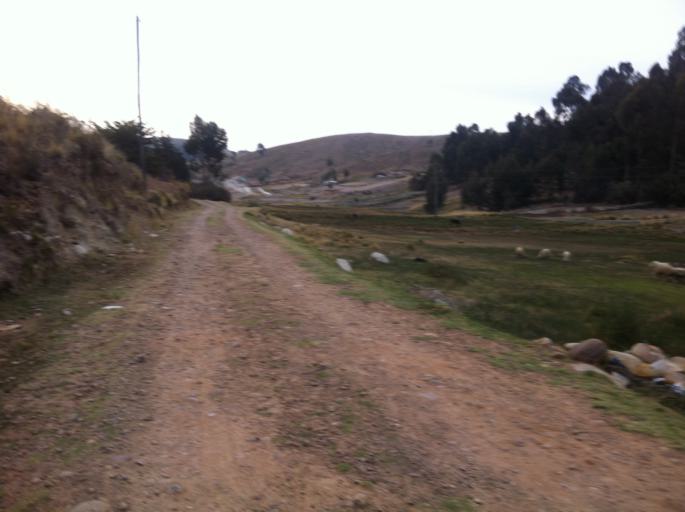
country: PE
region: Puno
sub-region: Yunguyo
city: Yunguyo
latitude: -16.1874
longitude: -69.0818
